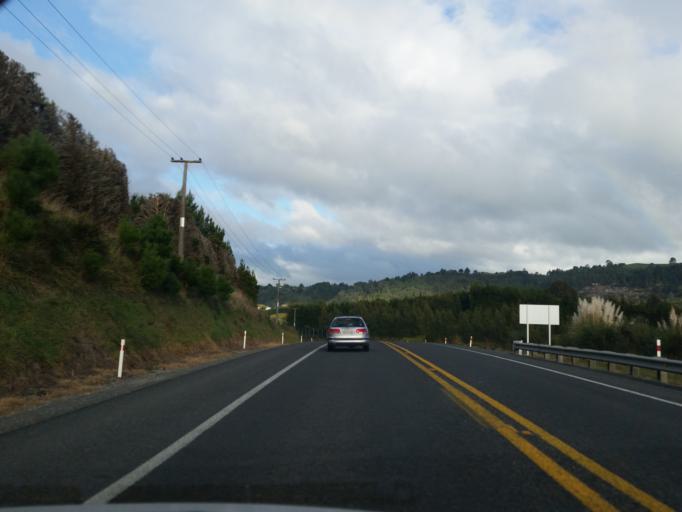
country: NZ
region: Bay of Plenty
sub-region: Tauranga City
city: Tauranga
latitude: -37.6892
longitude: 176.0407
